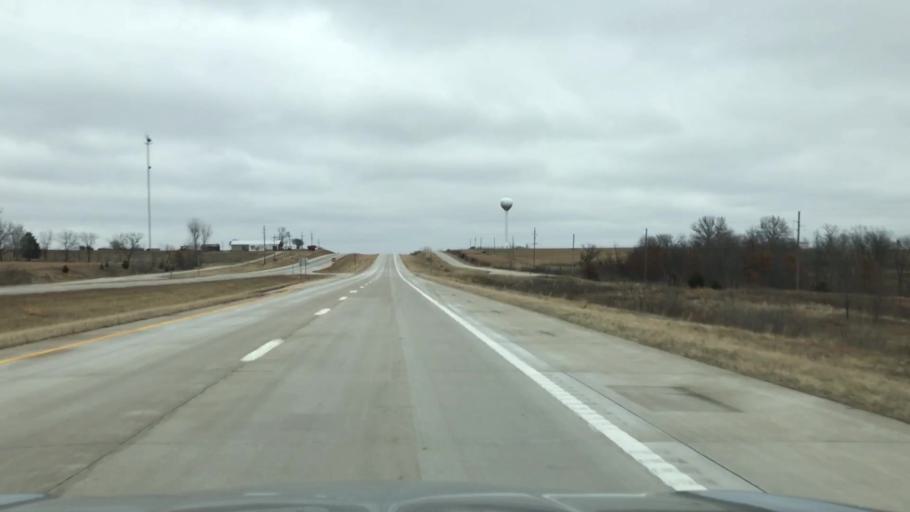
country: US
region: Missouri
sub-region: Livingston County
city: Chillicothe
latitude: 39.7392
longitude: -93.6655
